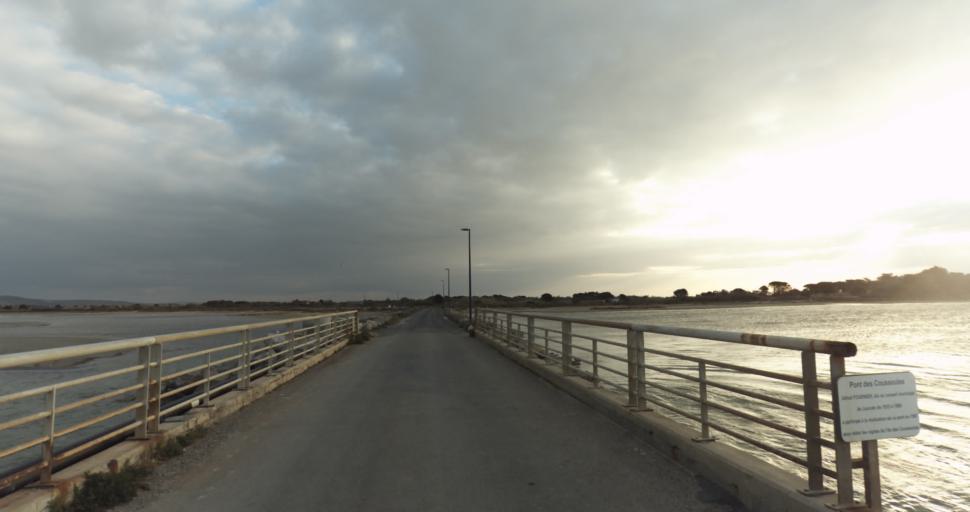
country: FR
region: Languedoc-Roussillon
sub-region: Departement de l'Aude
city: Leucate
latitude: 42.9385
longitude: 3.0265
